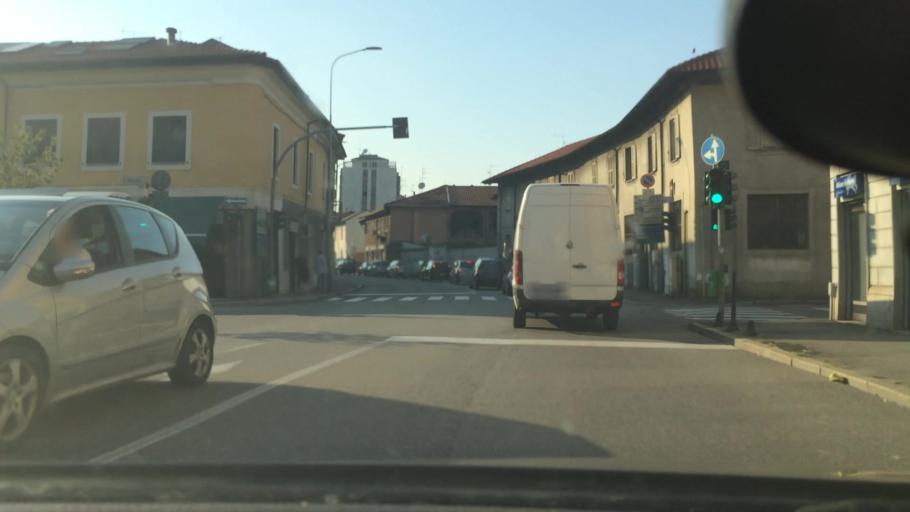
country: IT
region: Lombardy
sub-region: Citta metropolitana di Milano
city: Rho
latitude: 45.5292
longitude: 9.0464
